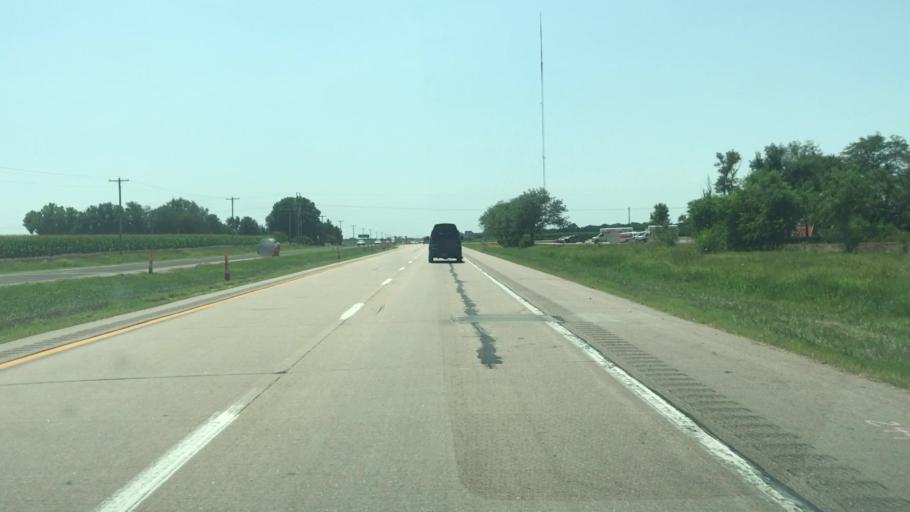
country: US
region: Nebraska
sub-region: Adams County
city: Hastings
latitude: 40.6574
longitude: -98.3824
